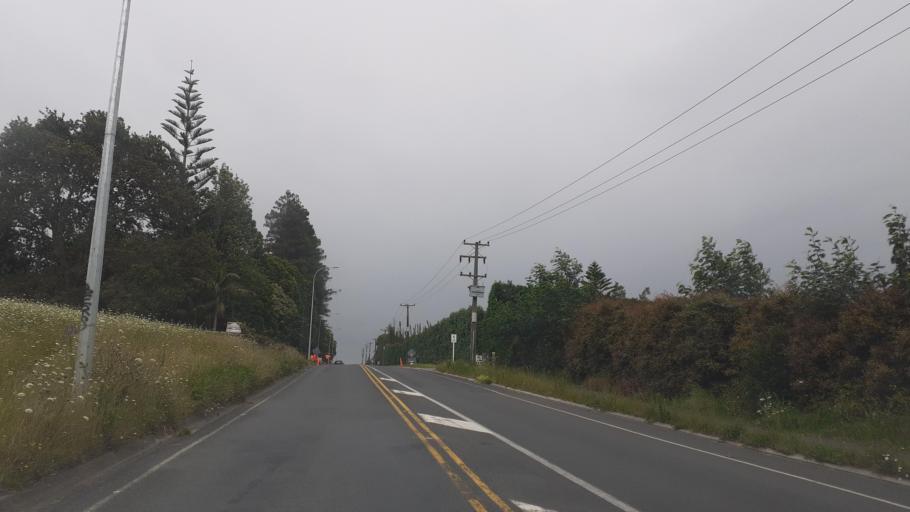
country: NZ
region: Northland
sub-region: Far North District
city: Kerikeri
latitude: -35.2399
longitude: 173.9382
